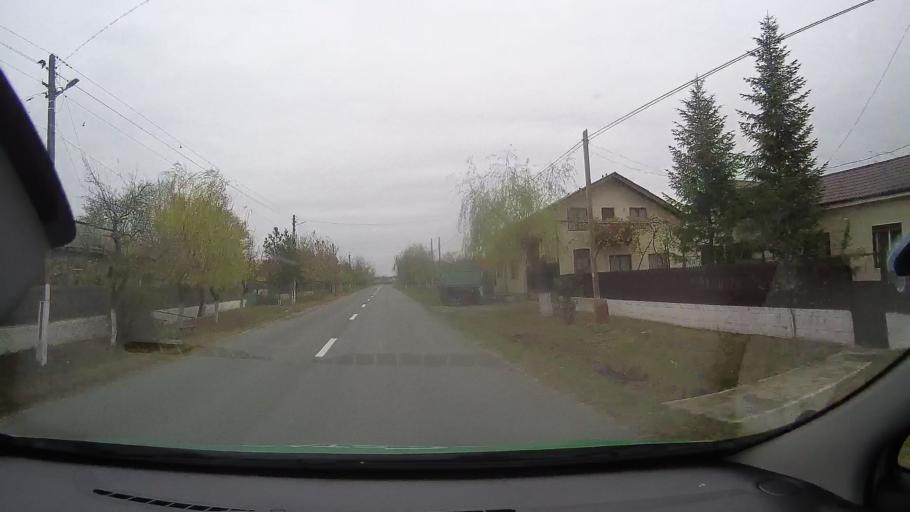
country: RO
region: Constanta
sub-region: Comuna Crucea
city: Crucea
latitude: 44.4489
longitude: 28.2412
